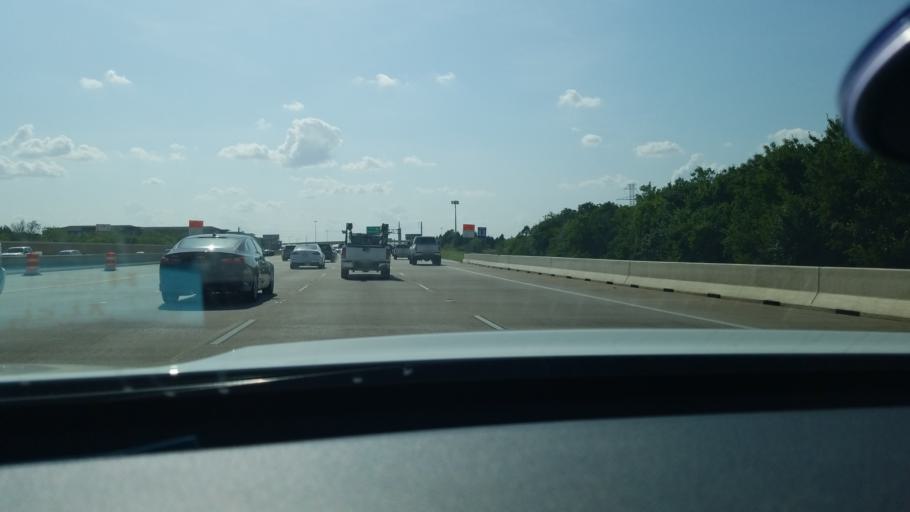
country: US
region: Texas
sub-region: Dallas County
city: Addison
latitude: 33.0129
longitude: -96.8176
